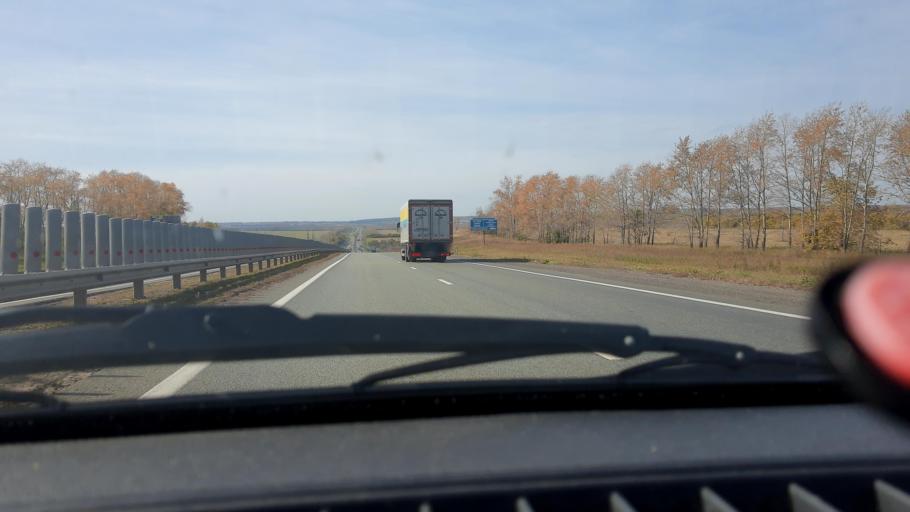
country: RU
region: Bashkortostan
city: Alekseyevka
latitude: 54.7308
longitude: 55.0345
